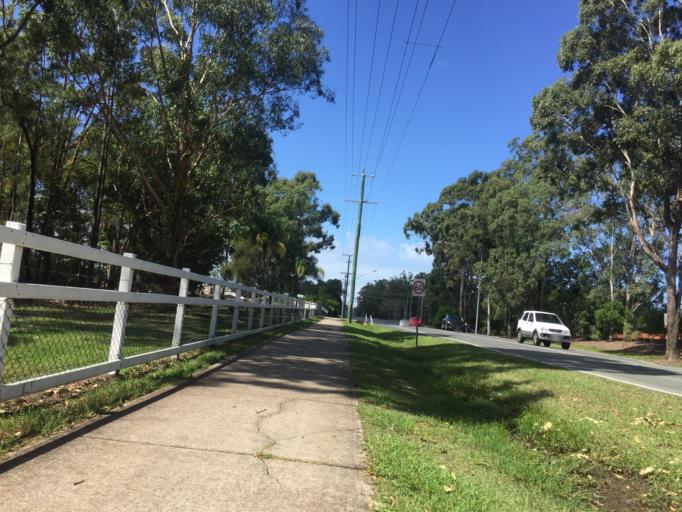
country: AU
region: Queensland
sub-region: Moreton Bay
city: Morayfield
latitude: -27.1112
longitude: 152.9410
